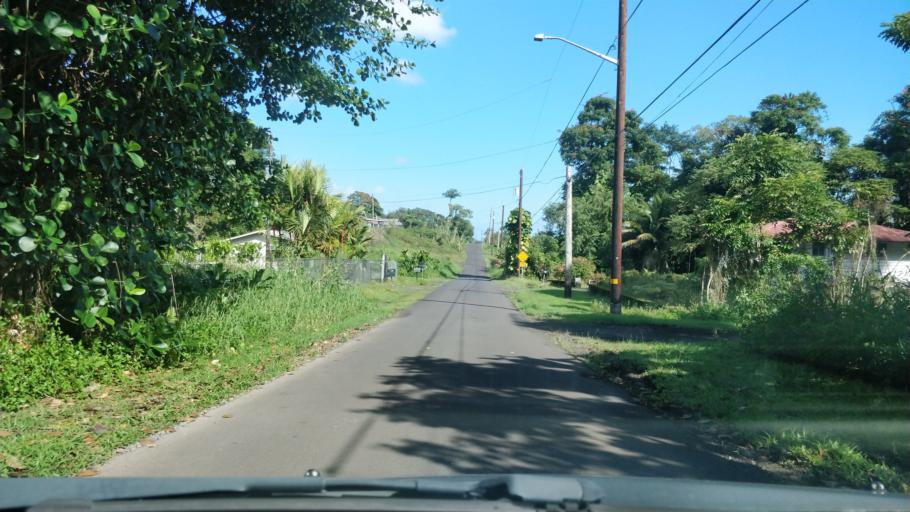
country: US
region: Hawaii
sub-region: Hawaii County
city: Kurtistown
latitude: 19.6596
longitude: -155.0991
